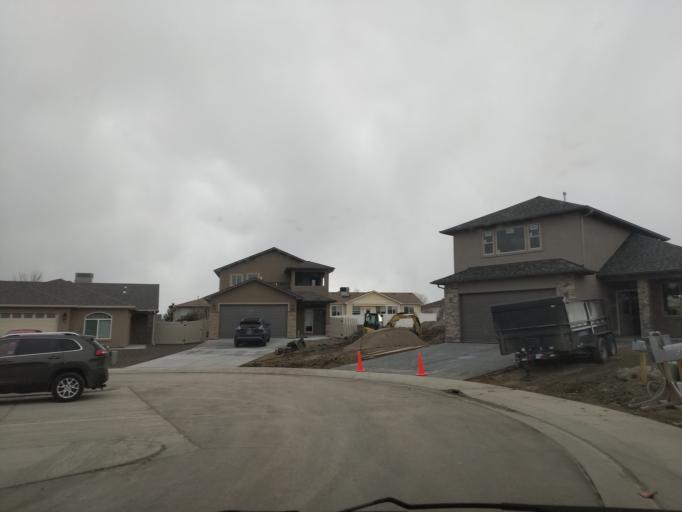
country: US
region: Colorado
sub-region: Mesa County
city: Fruitvale
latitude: 39.0903
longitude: -108.5221
